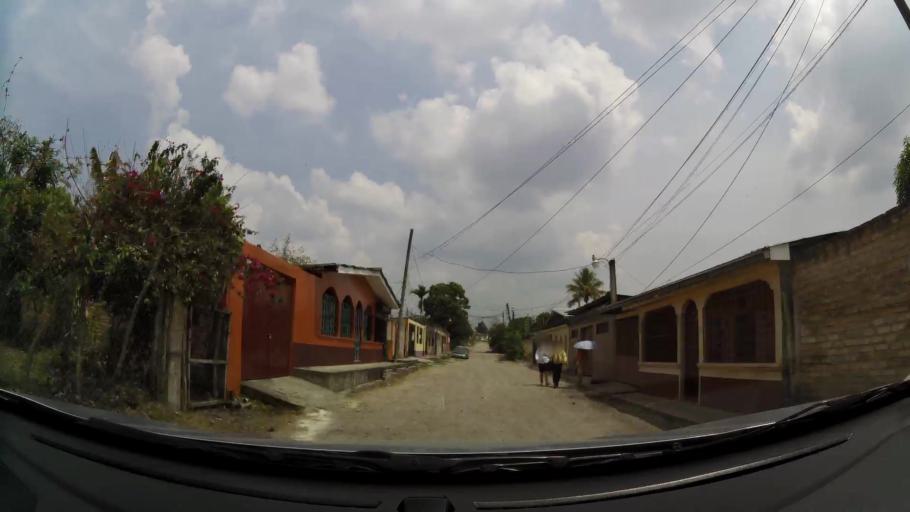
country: HN
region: Comayagua
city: Siguatepeque
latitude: 14.5997
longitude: -87.8273
